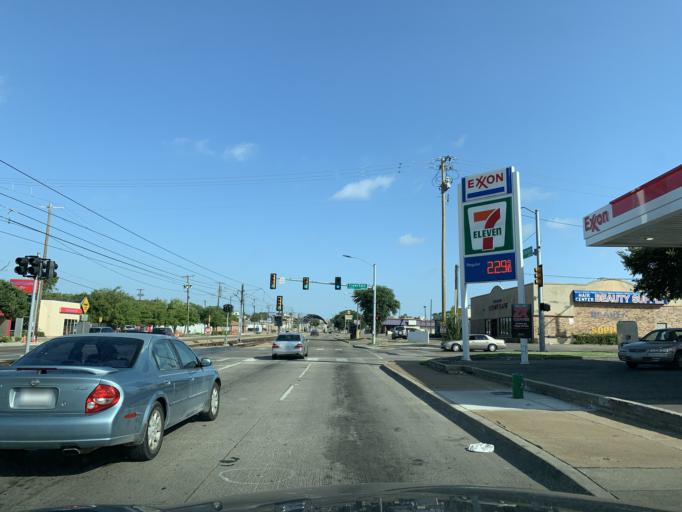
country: US
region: Texas
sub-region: Dallas County
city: Dallas
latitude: 32.7044
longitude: -96.7991
